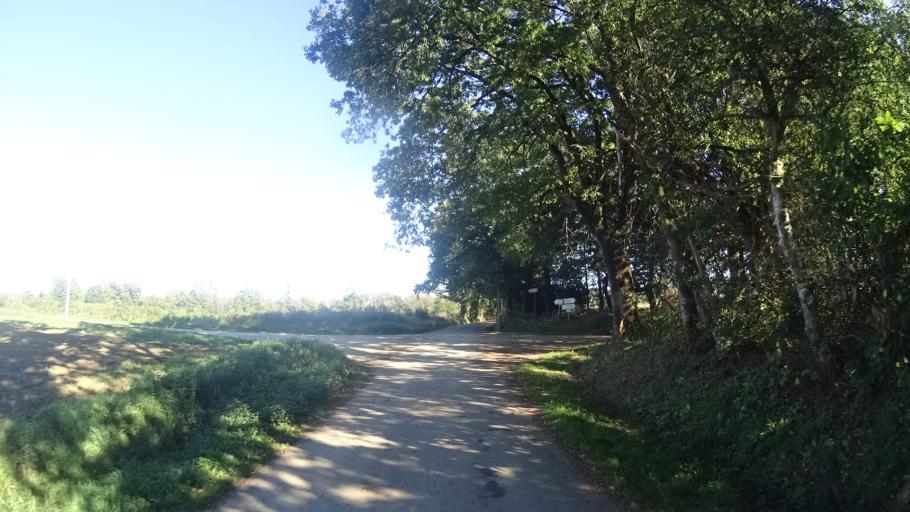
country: FR
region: Brittany
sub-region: Departement du Morbihan
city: Peillac
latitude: 47.7119
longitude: -2.2035
